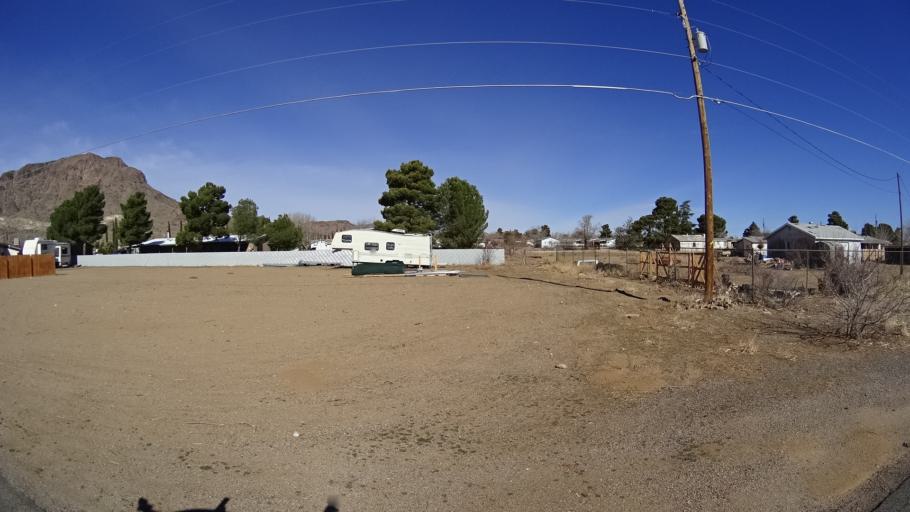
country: US
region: Arizona
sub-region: Mohave County
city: New Kingman-Butler
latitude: 35.2674
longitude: -114.0452
